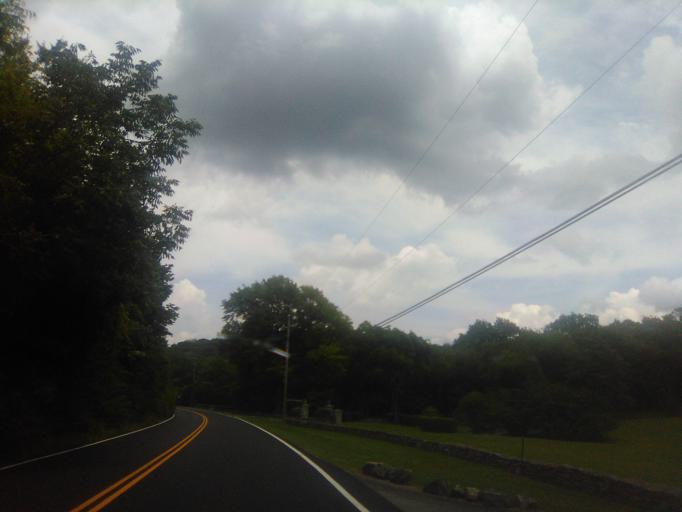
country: US
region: Tennessee
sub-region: Davidson County
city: Forest Hills
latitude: 36.0726
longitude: -86.8676
